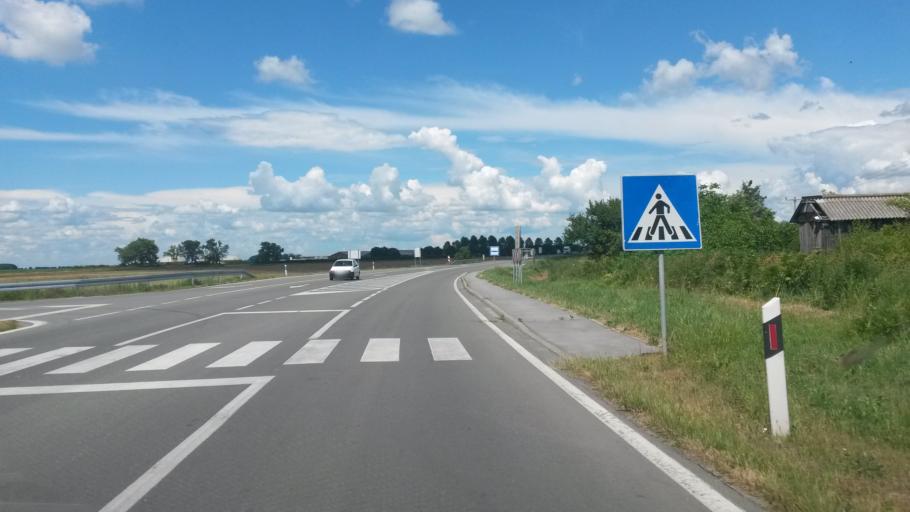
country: HR
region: Osjecko-Baranjska
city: Vuka
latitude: 45.4607
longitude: 18.5172
